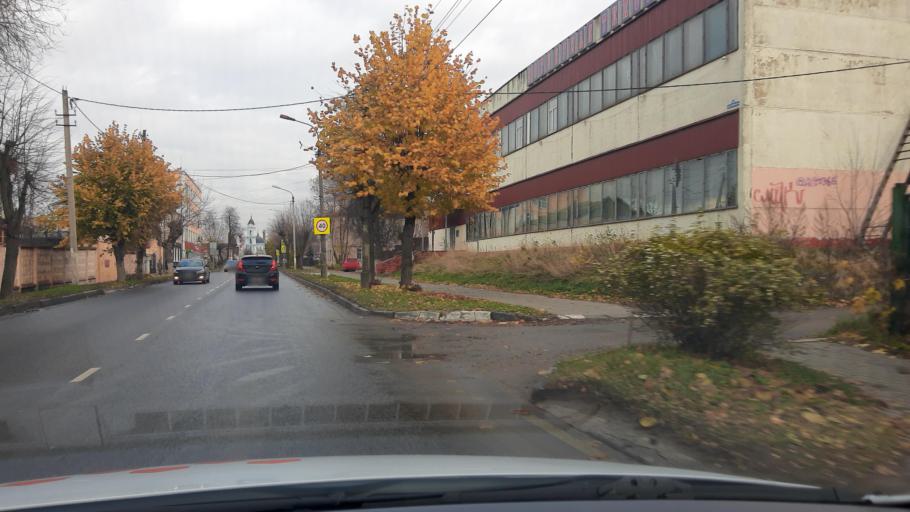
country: RU
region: Moskovskaya
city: Noginsk
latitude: 55.8539
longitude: 38.4291
